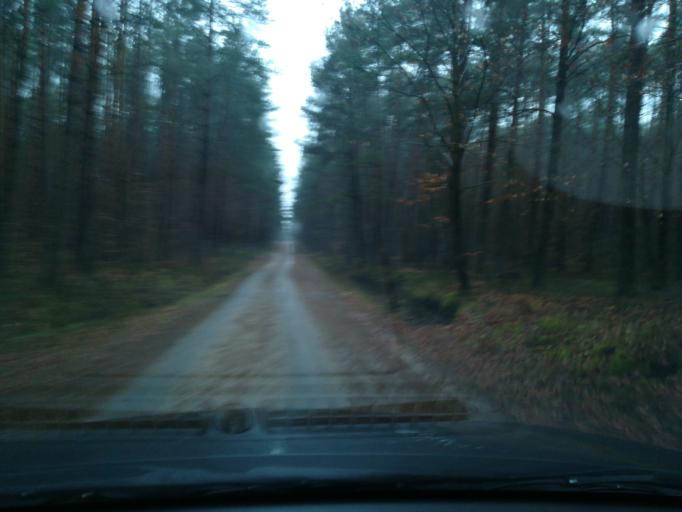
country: PL
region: Subcarpathian Voivodeship
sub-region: Powiat lancucki
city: Bialobrzegi
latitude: 50.1311
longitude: 22.3588
